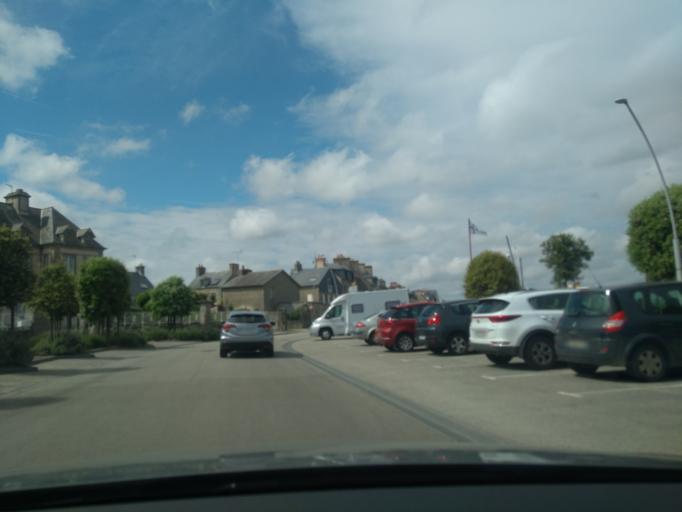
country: FR
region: Lower Normandy
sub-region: Departement de la Manche
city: Saint-Vaast-la-Hougue
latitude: 49.5898
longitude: -1.2662
